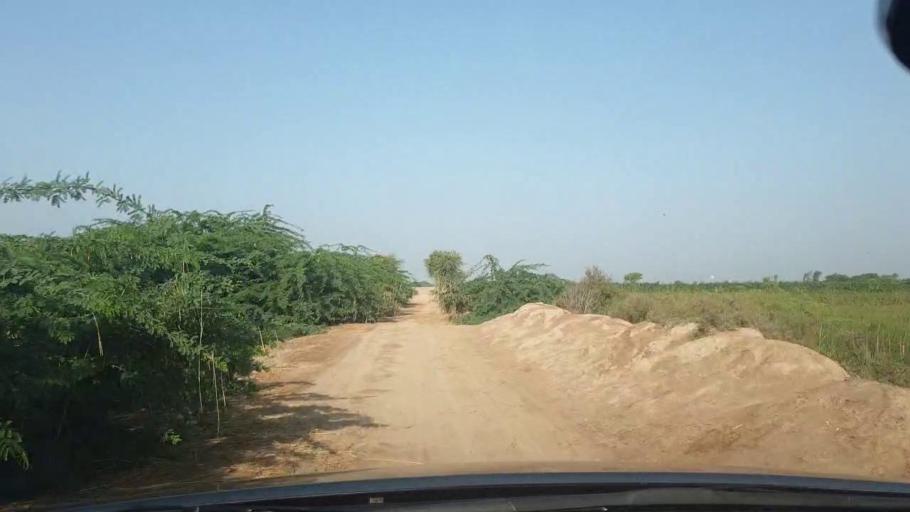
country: PK
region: Sindh
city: Tando Bago
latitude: 24.6452
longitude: 69.1336
